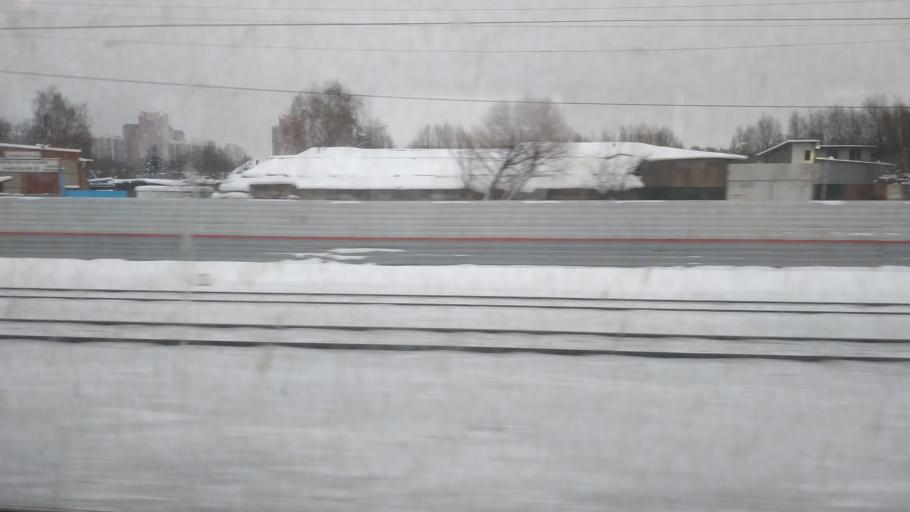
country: RU
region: Moscow
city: Annino
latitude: 55.5465
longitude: 37.5733
